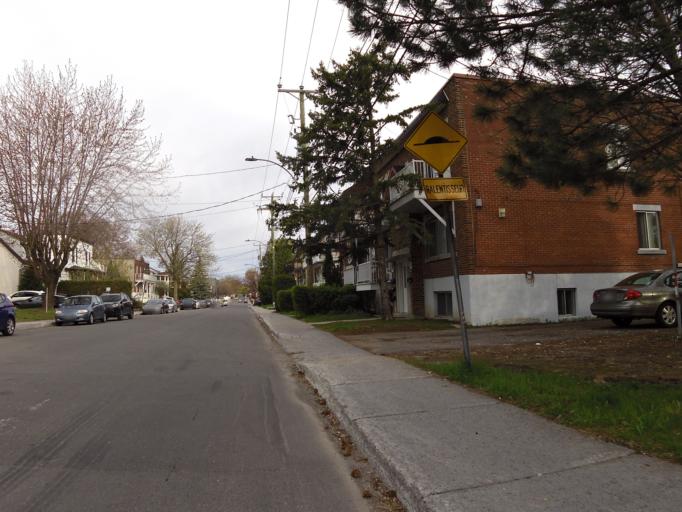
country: CA
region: Quebec
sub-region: Laval
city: Laval
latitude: 45.5420
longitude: -73.6917
